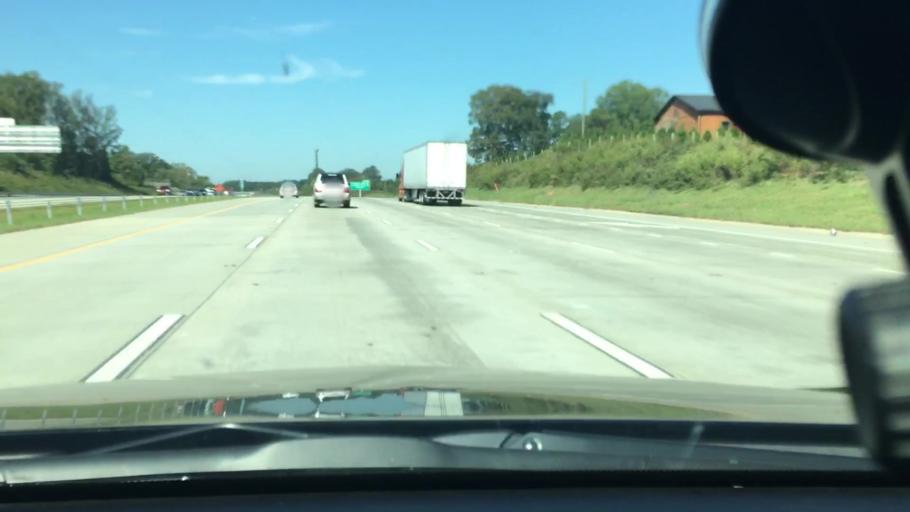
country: US
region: North Carolina
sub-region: Mecklenburg County
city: Huntersville
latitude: 35.3658
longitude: -80.7590
